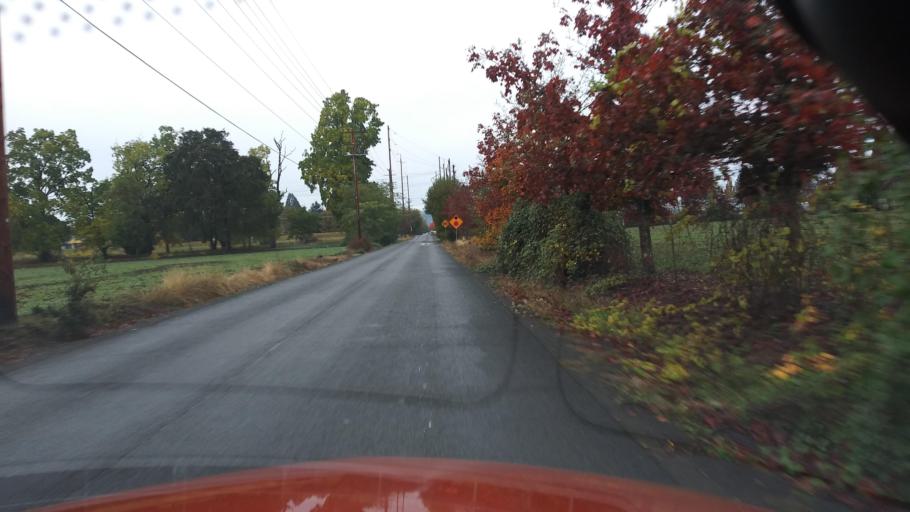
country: US
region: Oregon
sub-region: Washington County
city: Forest Grove
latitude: 45.5264
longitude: -123.0880
